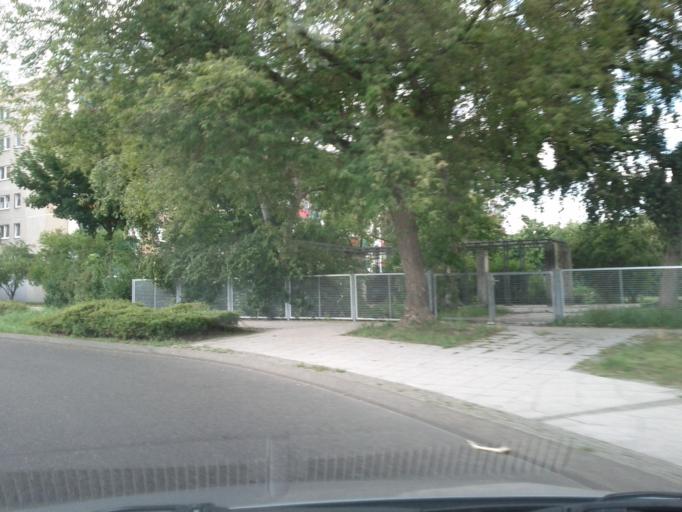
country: DE
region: Berlin
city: Marzahn
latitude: 52.5504
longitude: 13.5824
